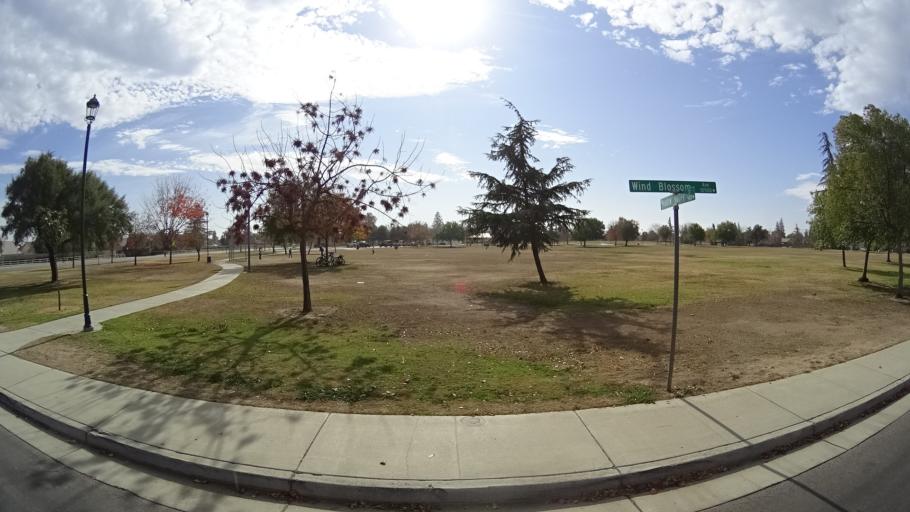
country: US
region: California
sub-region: Kern County
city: Greenacres
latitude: 35.4110
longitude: -119.1196
